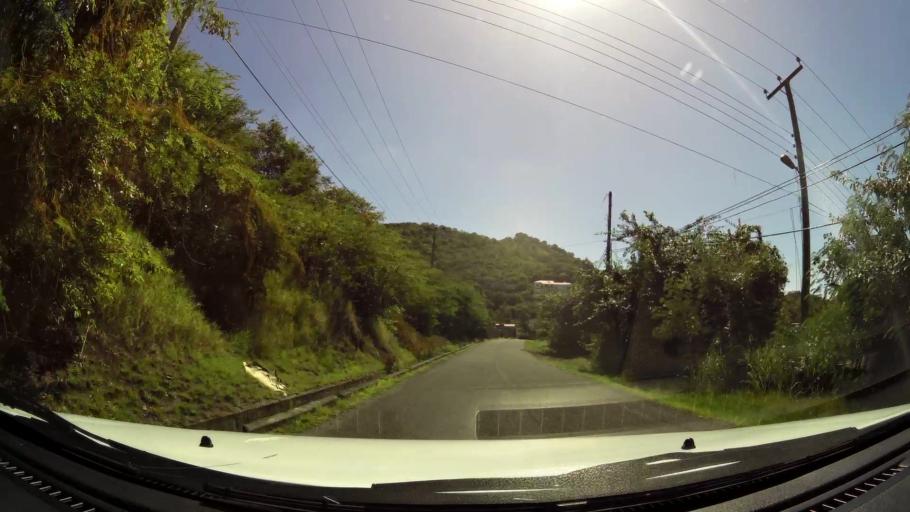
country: LC
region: Vieux-Fort
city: Vieux Fort
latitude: 13.7221
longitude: -60.9503
